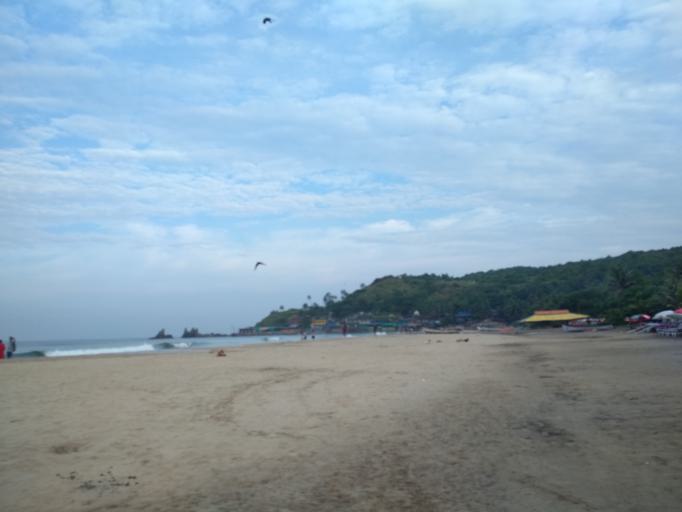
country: IN
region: Goa
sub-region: North Goa
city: Arambol
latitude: 15.6894
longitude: 73.7022
